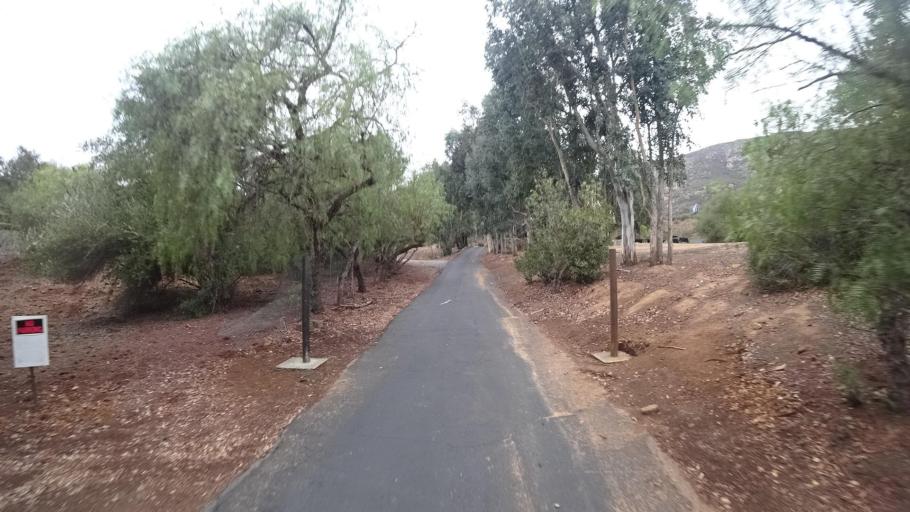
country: US
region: California
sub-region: San Diego County
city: Escondido
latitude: 33.0649
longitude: -117.1228
